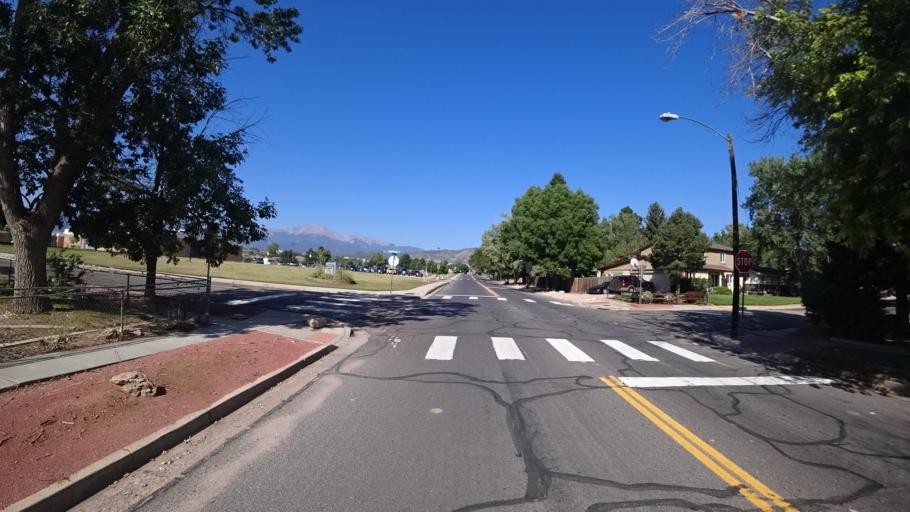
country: US
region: Colorado
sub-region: El Paso County
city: Colorado Springs
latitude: 38.8931
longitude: -104.8384
